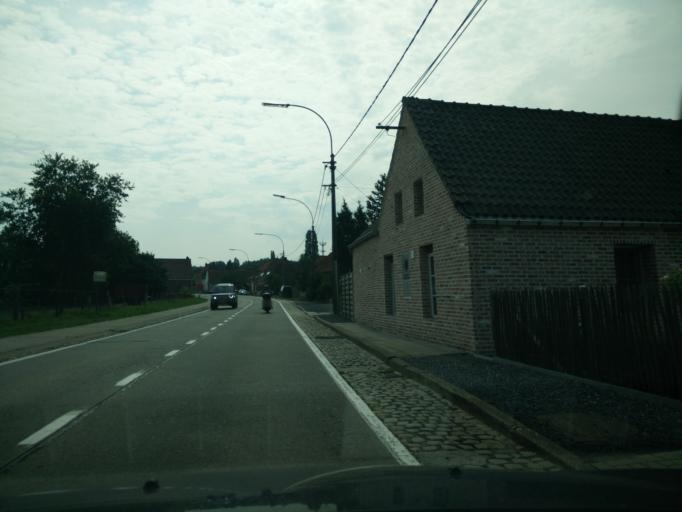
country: BE
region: Flanders
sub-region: Provincie Oost-Vlaanderen
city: Merelbeke
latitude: 50.9466
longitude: 3.7347
